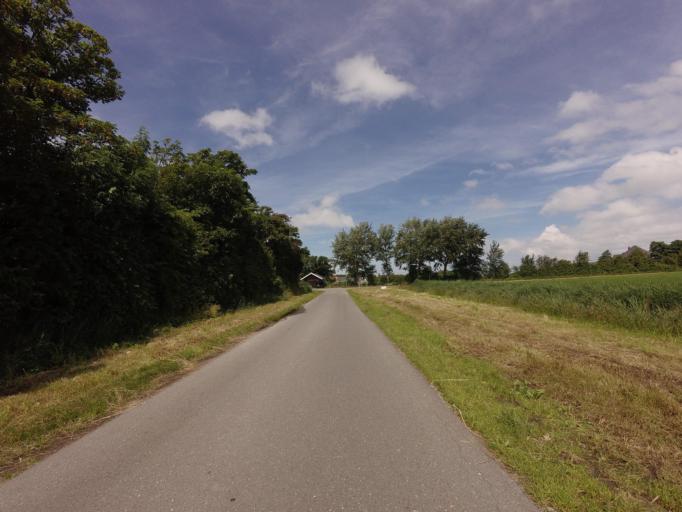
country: NL
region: North Holland
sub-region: Gemeente Texel
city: Den Burg
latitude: 53.0828
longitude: 4.8798
